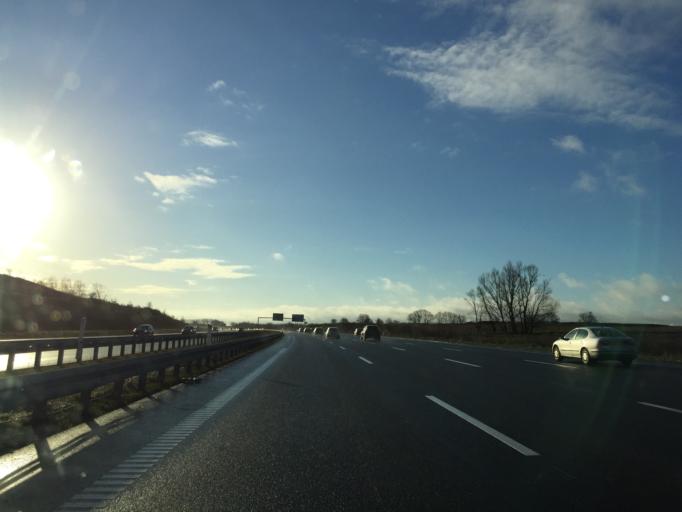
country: DK
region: Zealand
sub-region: Solrod Kommune
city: Solrod
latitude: 55.5333
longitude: 12.1980
